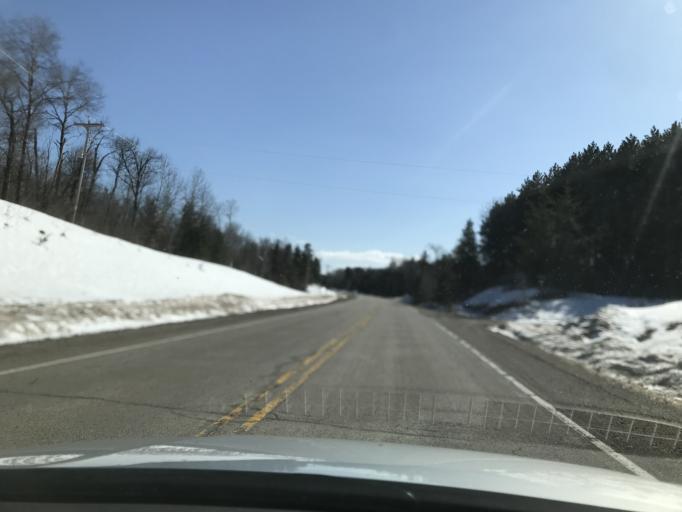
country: US
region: Wisconsin
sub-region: Marinette County
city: Niagara
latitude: 45.3346
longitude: -88.1013
